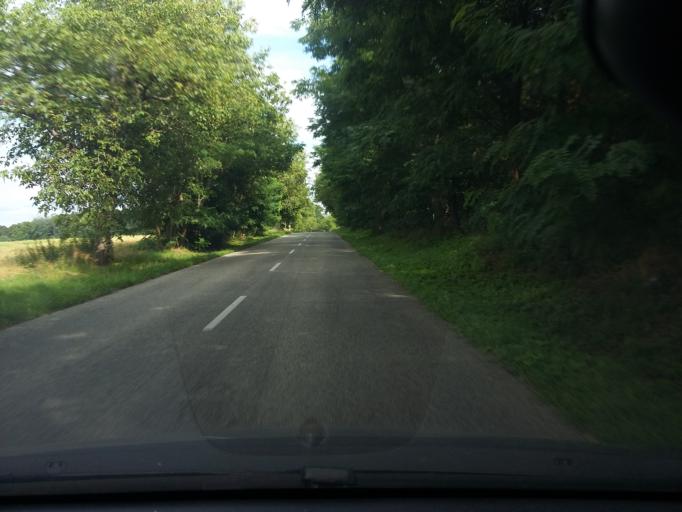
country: SK
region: Trnavsky
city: Gbely
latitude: 48.5744
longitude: 17.2003
